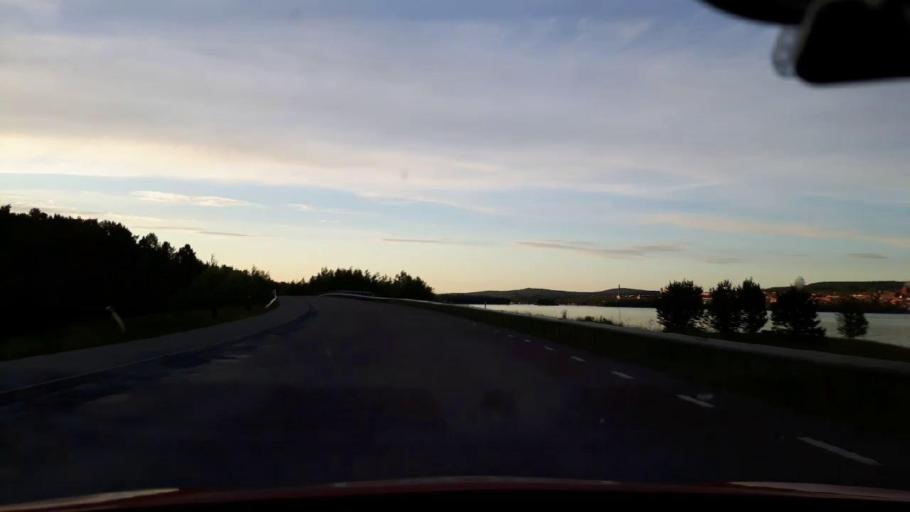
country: SE
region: Jaemtland
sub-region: OEstersunds Kommun
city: Ostersund
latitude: 63.1655
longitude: 14.6084
